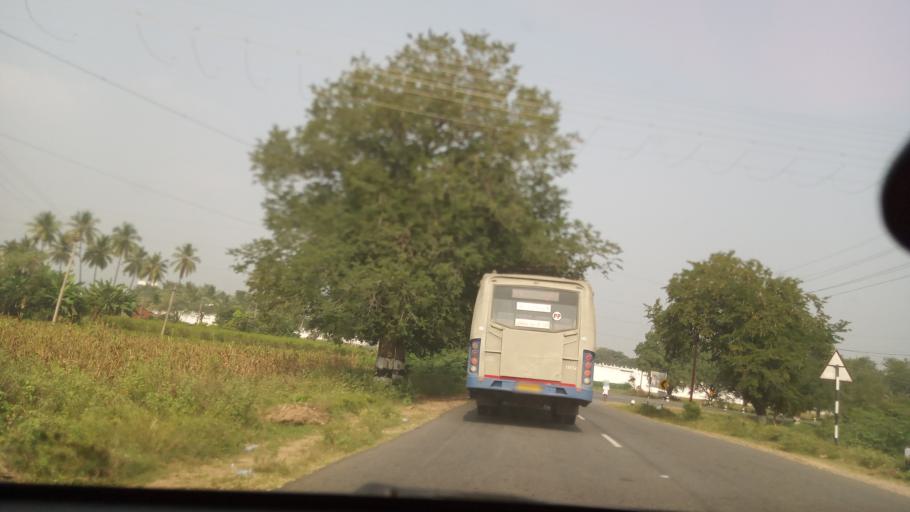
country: IN
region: Tamil Nadu
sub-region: Erode
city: Punjai Puliyampatti
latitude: 11.4205
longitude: 77.1944
